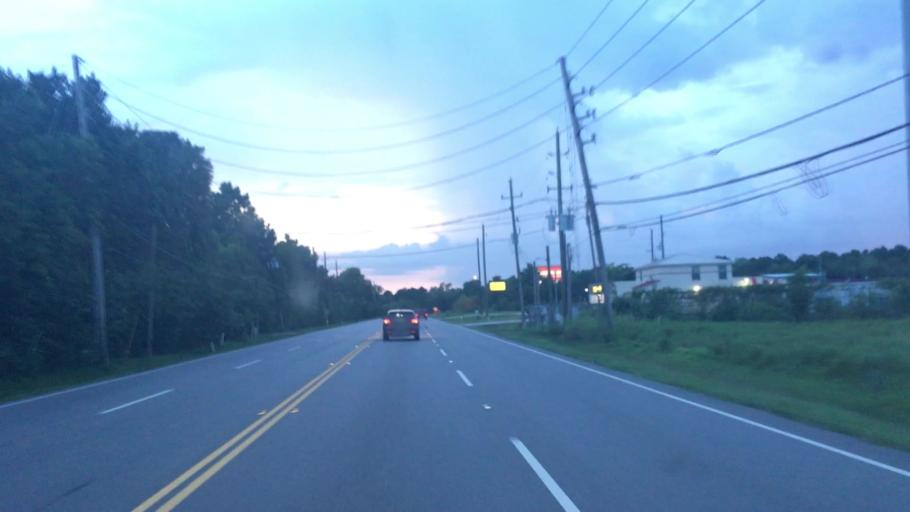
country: US
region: Texas
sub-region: Harris County
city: Humble
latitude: 29.9646
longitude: -95.2415
